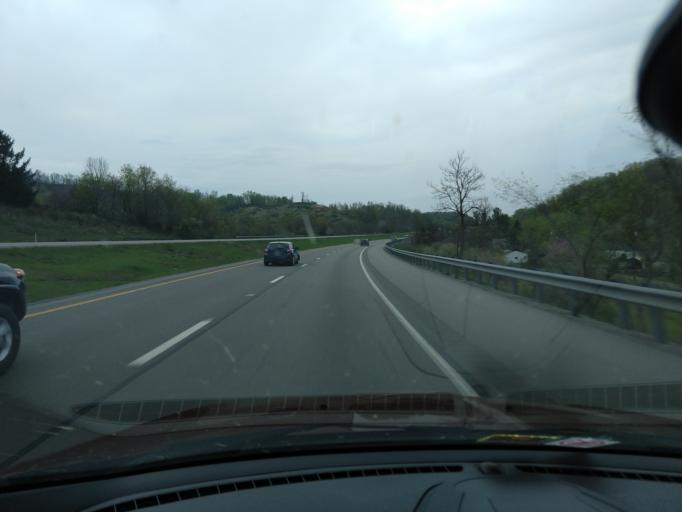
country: US
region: West Virginia
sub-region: Lewis County
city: Weston
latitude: 39.1284
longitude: -80.3845
